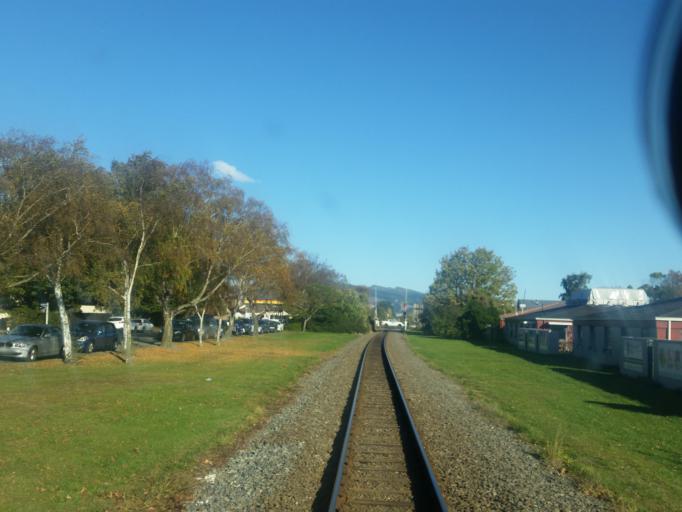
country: NZ
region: Canterbury
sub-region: Christchurch City
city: Christchurch
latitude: -43.5273
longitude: 172.6084
